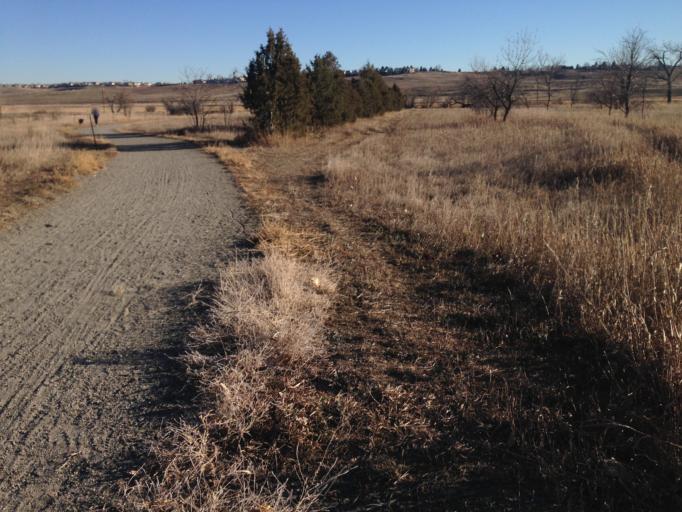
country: US
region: Colorado
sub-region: Broomfield County
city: Broomfield
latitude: 39.9444
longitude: -105.1044
